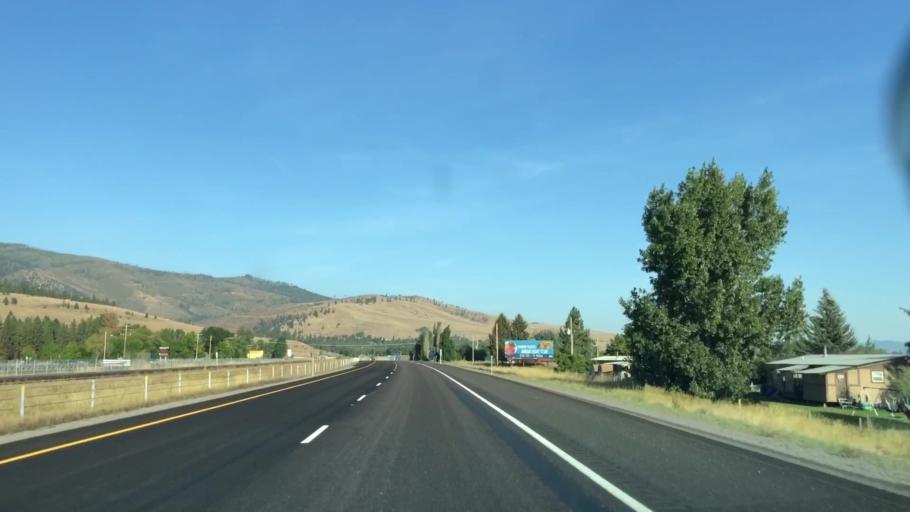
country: US
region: Montana
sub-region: Missoula County
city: Frenchtown
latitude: 47.0187
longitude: -114.2463
